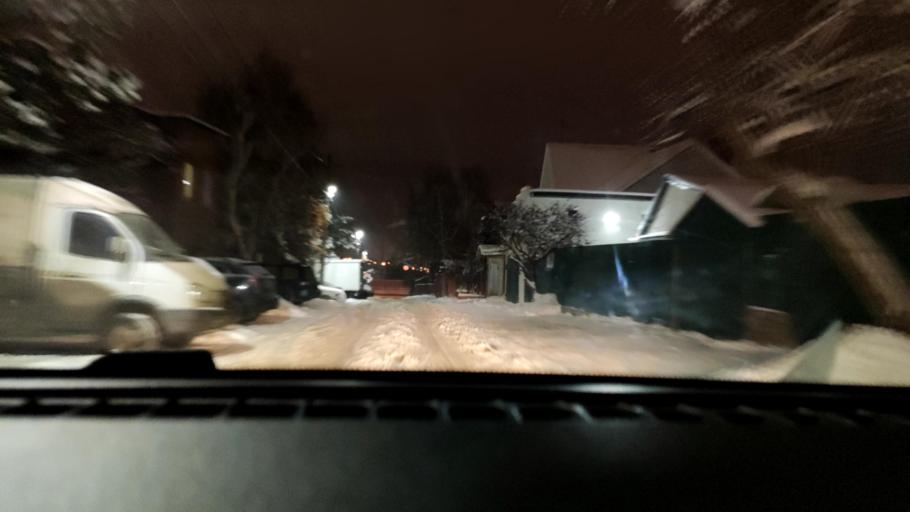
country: RU
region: Samara
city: Samara
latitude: 53.1801
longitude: 50.1893
